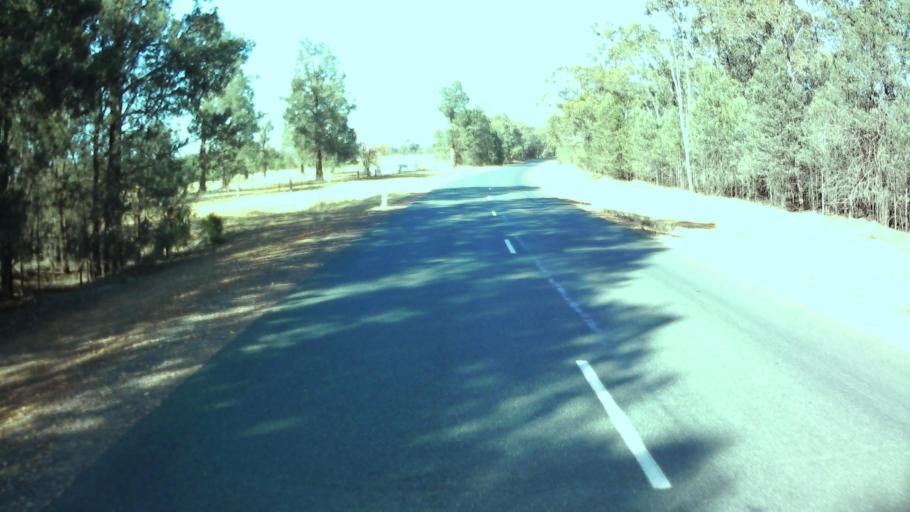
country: AU
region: New South Wales
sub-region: Weddin
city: Grenfell
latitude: -34.0336
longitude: 148.0893
